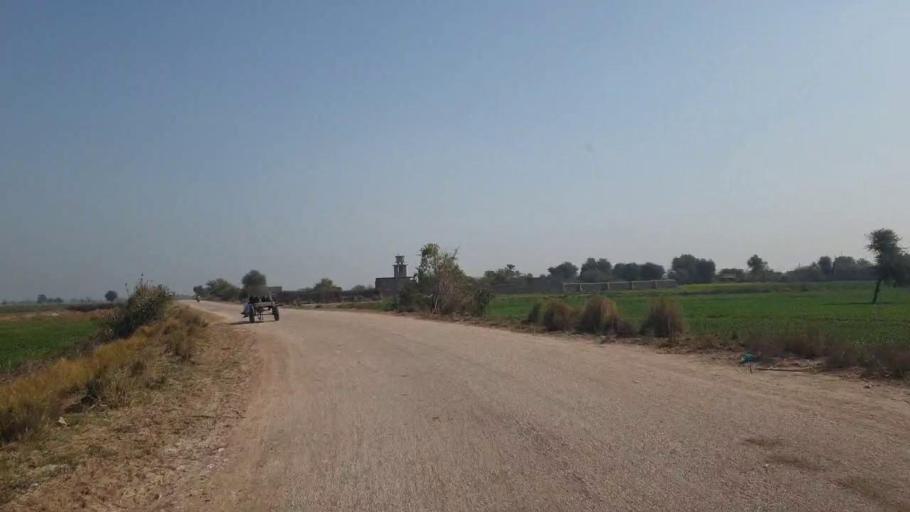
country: PK
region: Sindh
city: Sakrand
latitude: 26.0405
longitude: 68.4305
